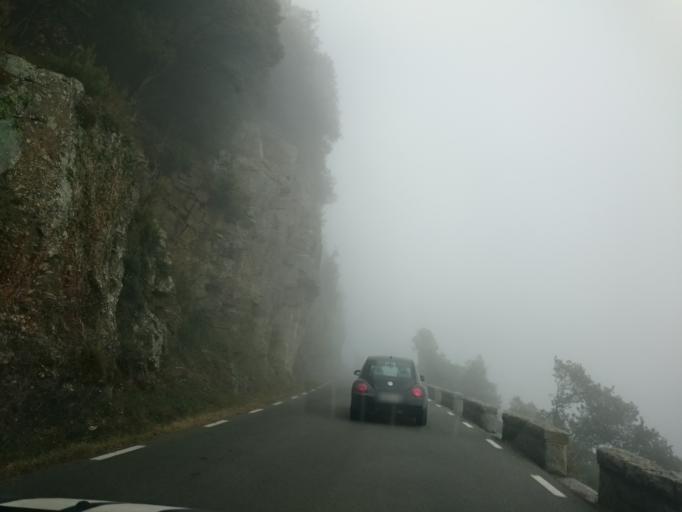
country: ES
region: Catalonia
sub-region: Provincia de Barcelona
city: Fogars de Montclus
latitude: 41.7550
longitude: 2.4725
